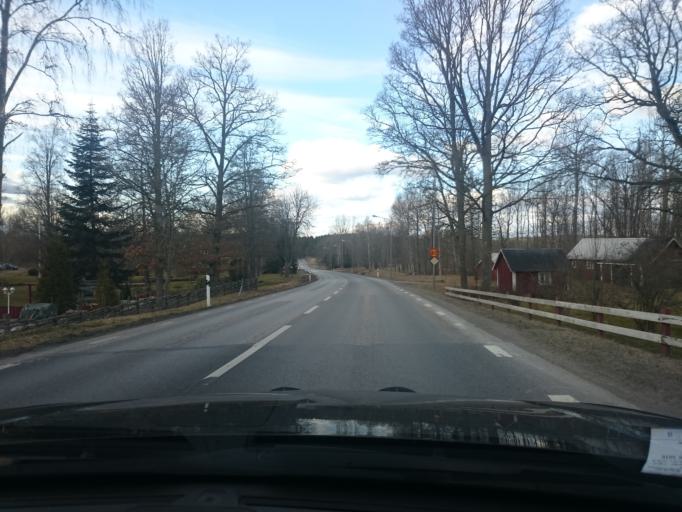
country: SE
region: Joenkoeping
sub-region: Vetlanda Kommun
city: Vetlanda
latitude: 57.3148
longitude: 15.1213
